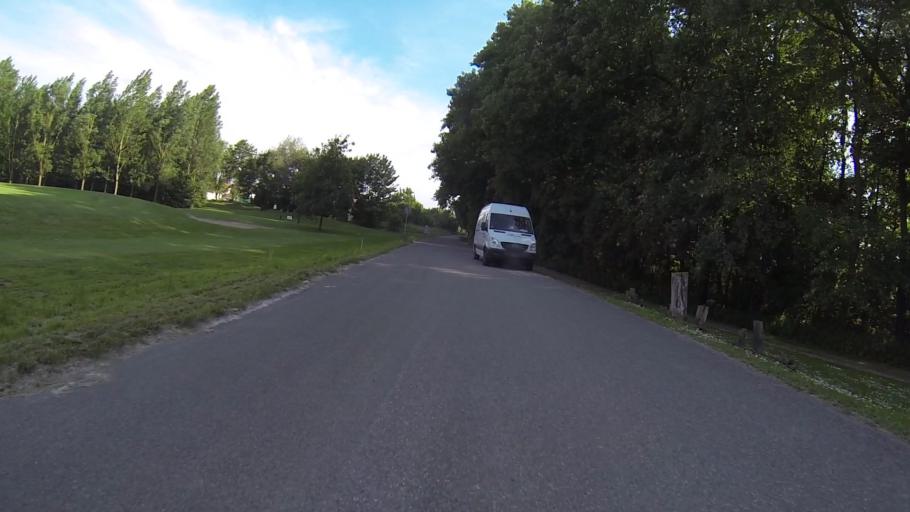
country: DE
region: Bavaria
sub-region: Swabia
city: Neu-Ulm
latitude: 48.4140
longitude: 10.0183
